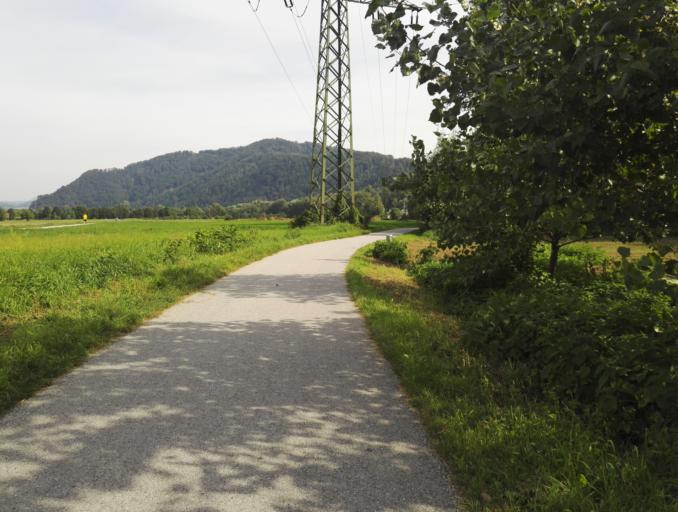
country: AT
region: Styria
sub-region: Politischer Bezirk Graz-Umgebung
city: Gratwein
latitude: 47.1359
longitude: 15.3246
